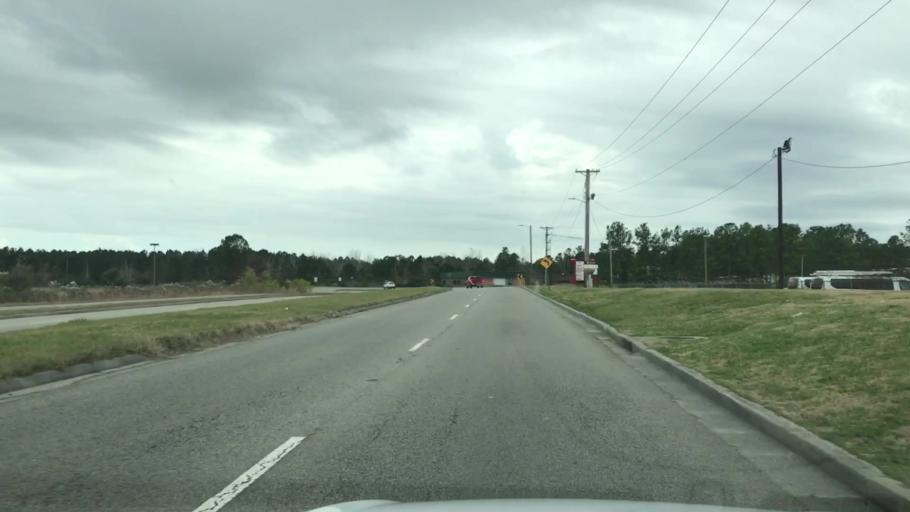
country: US
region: South Carolina
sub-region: Horry County
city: Forestbrook
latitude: 33.7114
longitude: -78.9395
